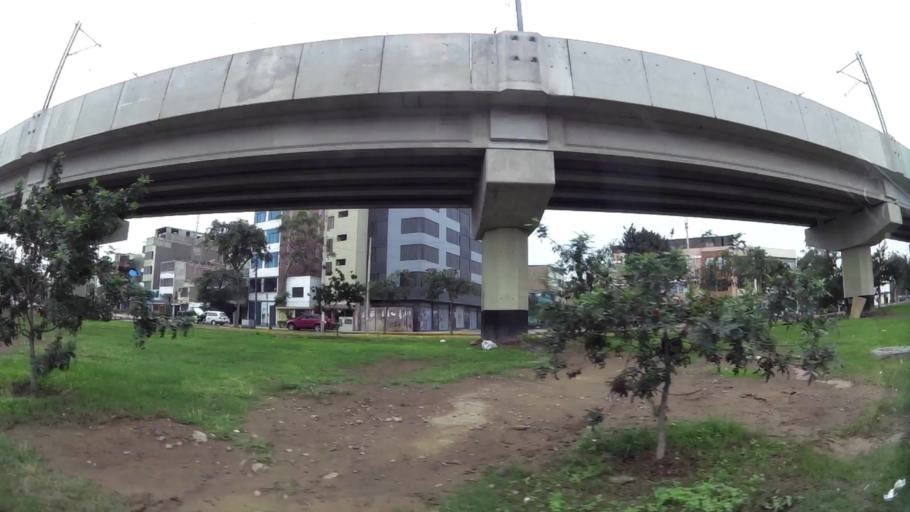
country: PE
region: Lima
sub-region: Lima
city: San Luis
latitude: -12.0791
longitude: -77.0101
